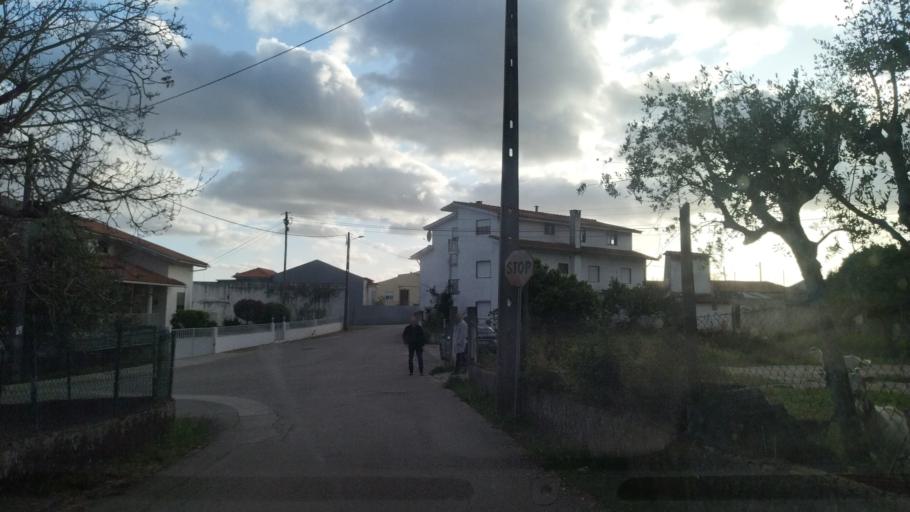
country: PT
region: Coimbra
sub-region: Coimbra
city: Coimbra
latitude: 40.1651
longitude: -8.4489
